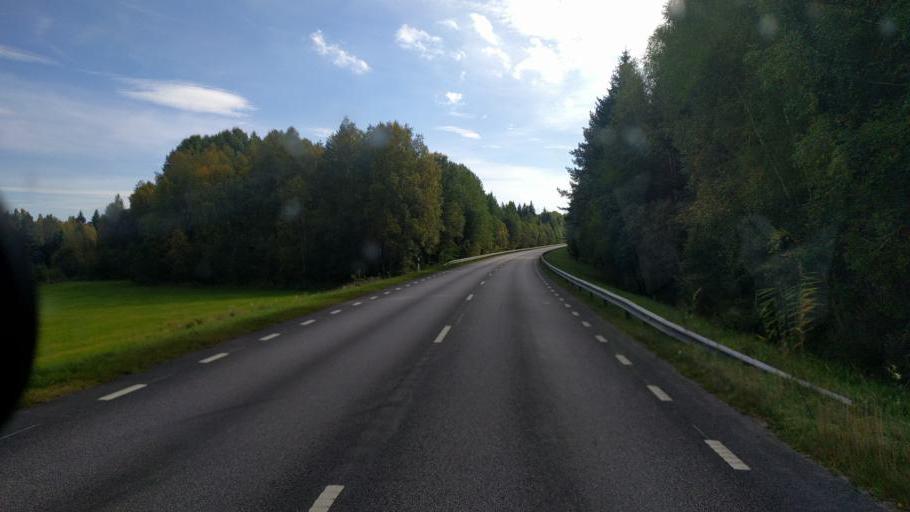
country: SE
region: OEstergoetland
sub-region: Kinda Kommun
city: Kisa
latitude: 57.9488
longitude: 15.6654
